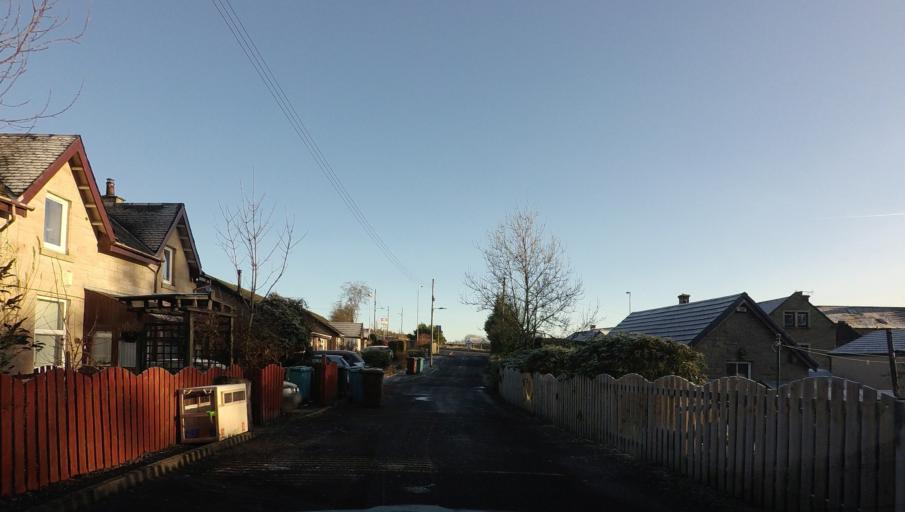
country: GB
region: Scotland
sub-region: North Lanarkshire
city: Shotts
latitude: 55.8107
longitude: -3.8396
